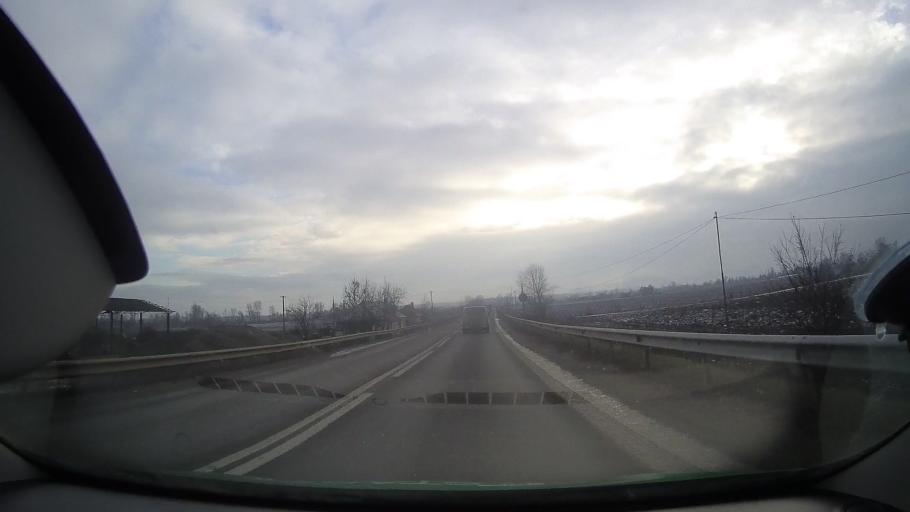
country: RO
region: Mures
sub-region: Comuna Cuci
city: Cuci
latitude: 46.4751
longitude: 24.1447
